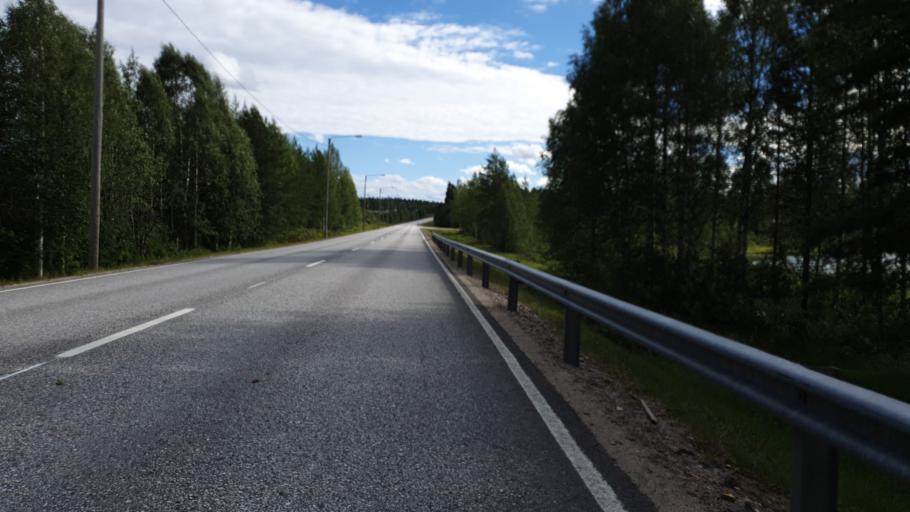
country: FI
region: Kainuu
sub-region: Kehys-Kainuu
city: Kuhmo
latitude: 64.5420
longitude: 29.9619
